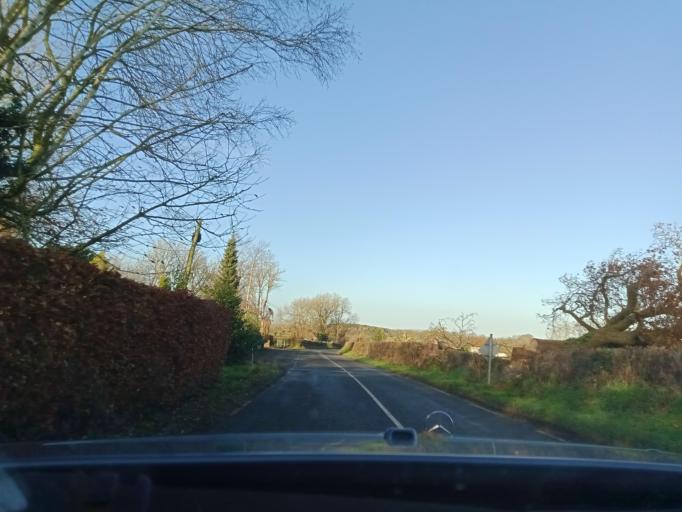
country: IE
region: Leinster
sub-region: Kilkenny
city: Callan
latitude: 52.5124
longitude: -7.3852
